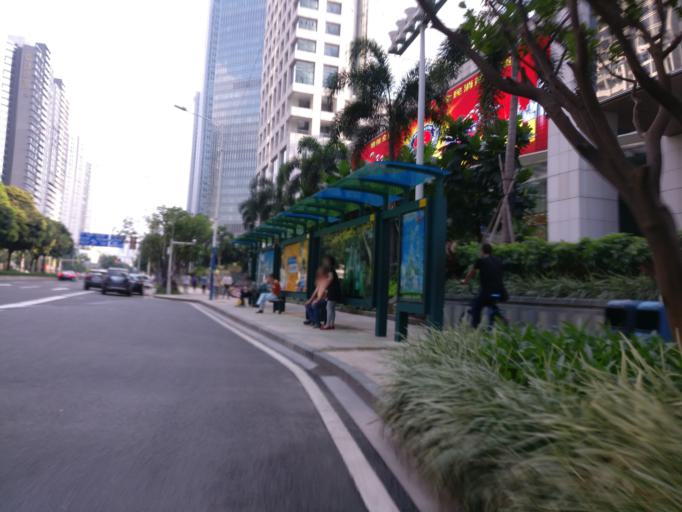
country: CN
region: Guangdong
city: Wushan
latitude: 23.1231
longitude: 113.3223
